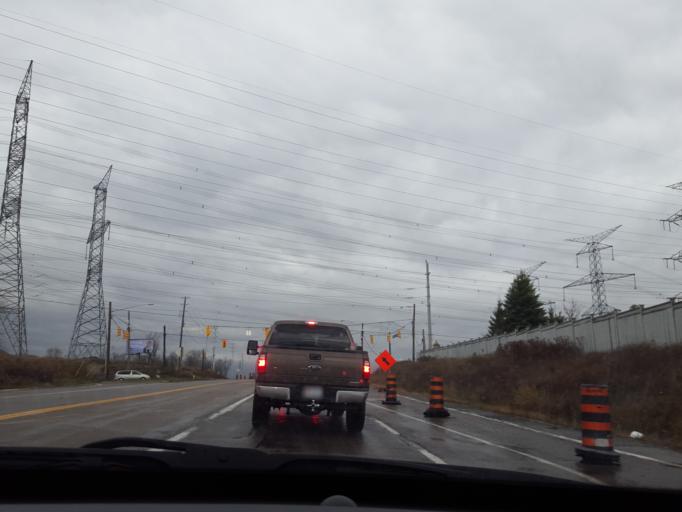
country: CA
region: Ontario
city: Ajax
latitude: 43.8668
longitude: -79.0826
